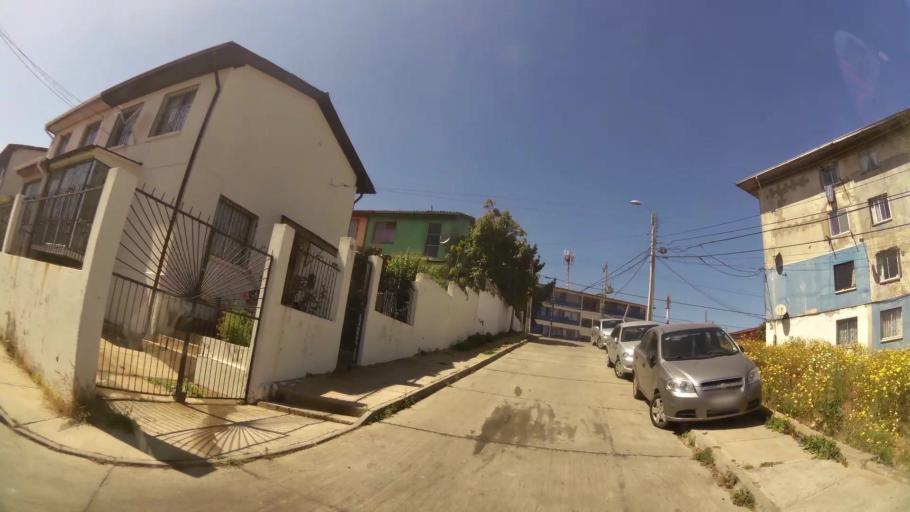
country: CL
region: Valparaiso
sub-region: Provincia de Valparaiso
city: Valparaiso
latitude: -33.0405
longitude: -71.6509
